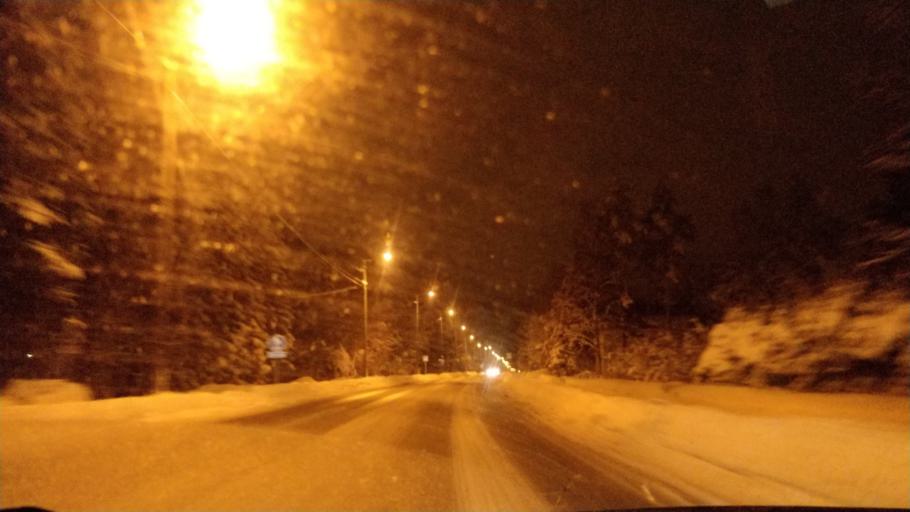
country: FI
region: Lapland
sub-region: Rovaniemi
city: Rovaniemi
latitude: 66.3737
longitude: 25.3825
